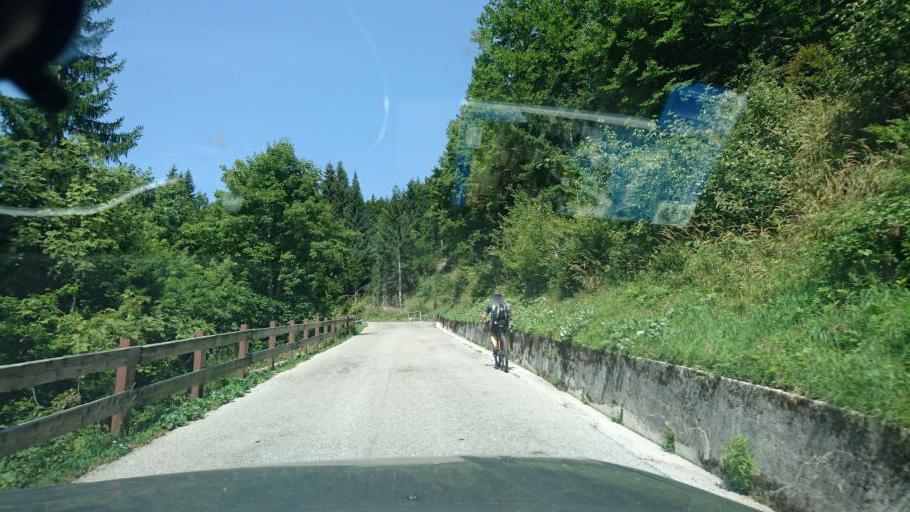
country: SI
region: Bovec
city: Bovec
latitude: 46.3957
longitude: 13.4649
